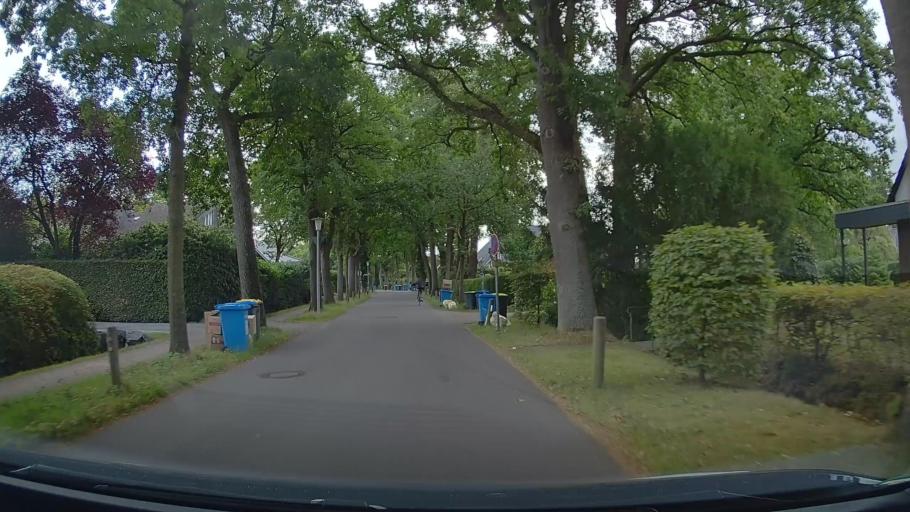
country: DE
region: Lower Saxony
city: Oldenburg
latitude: 53.1497
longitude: 8.1692
